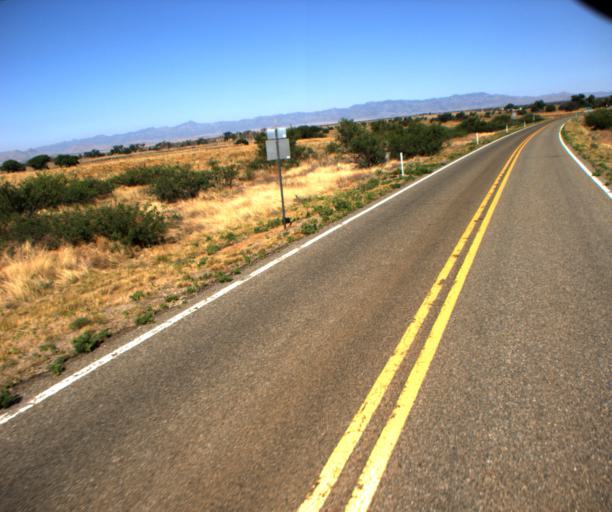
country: US
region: Arizona
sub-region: Graham County
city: Swift Trail Junction
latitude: 32.5827
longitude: -109.9561
